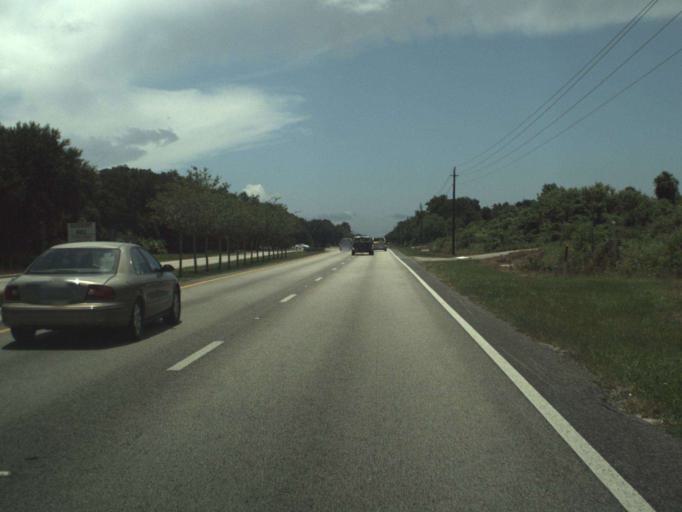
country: US
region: Florida
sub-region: Indian River County
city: Sebastian
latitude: 27.8000
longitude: -80.4618
